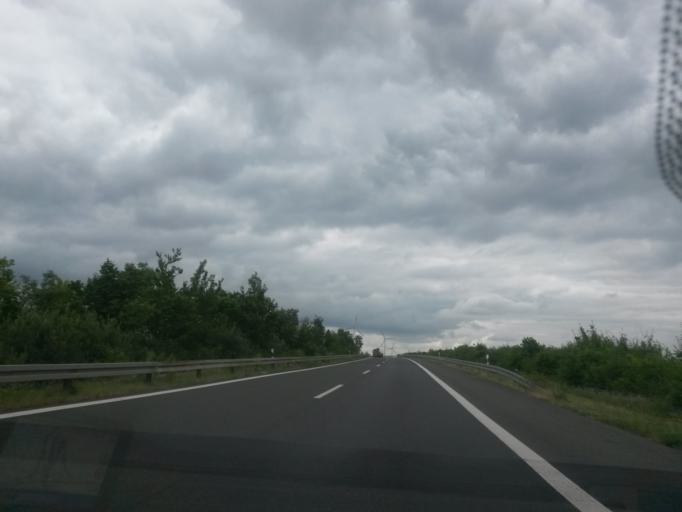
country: DE
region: Bavaria
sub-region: Regierungsbezirk Unterfranken
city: Biebelried
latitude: 49.7828
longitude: 10.0870
